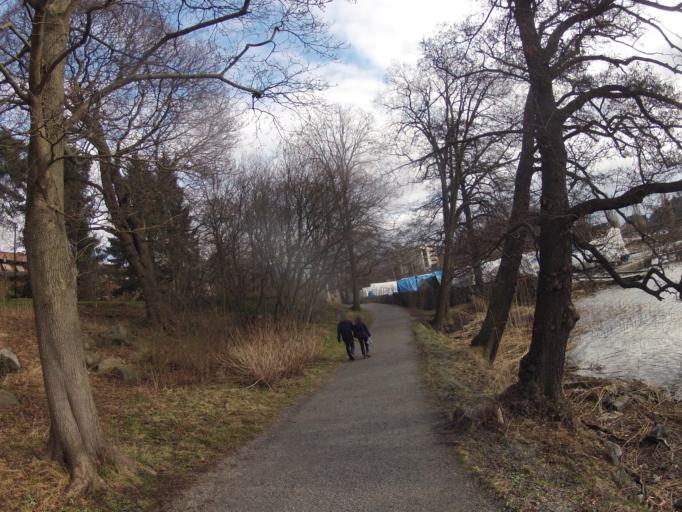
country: SE
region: Stockholm
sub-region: Stockholms Kommun
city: Stockholm
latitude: 59.3560
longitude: 18.0520
